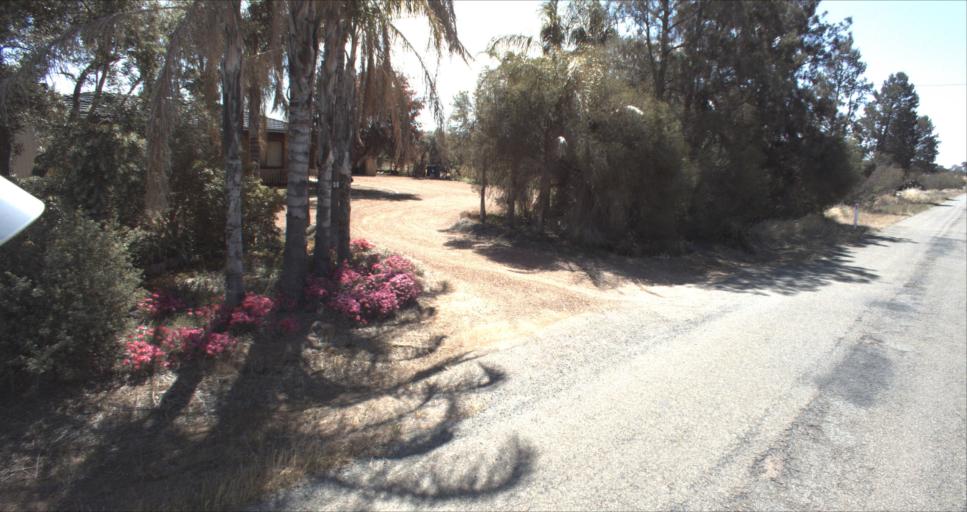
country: AU
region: New South Wales
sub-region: Leeton
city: Leeton
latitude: -34.5916
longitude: 146.4407
